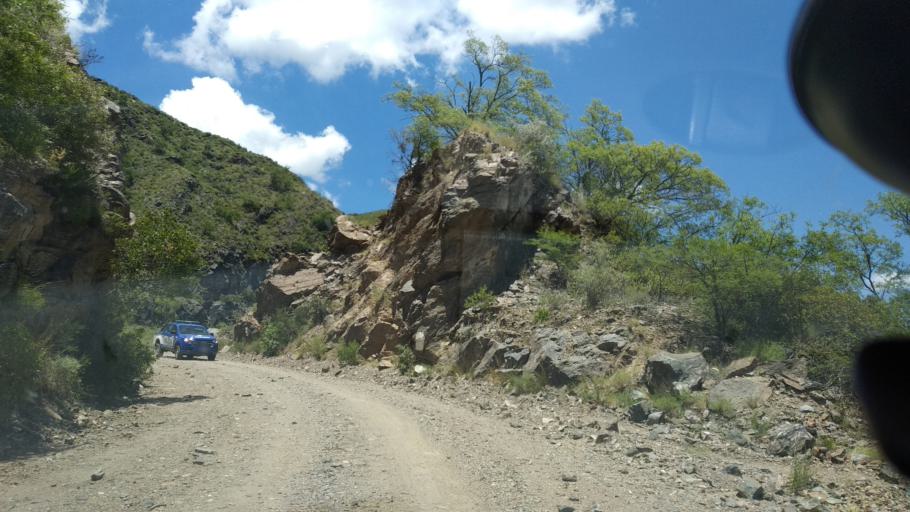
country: AR
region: Cordoba
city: Salsacate
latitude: -31.3703
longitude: -65.4080
